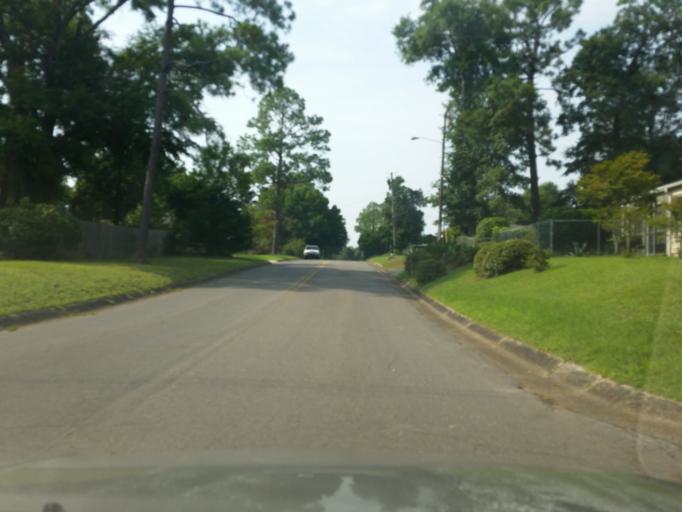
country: US
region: Florida
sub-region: Escambia County
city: Goulding
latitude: 30.4487
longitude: -87.2006
